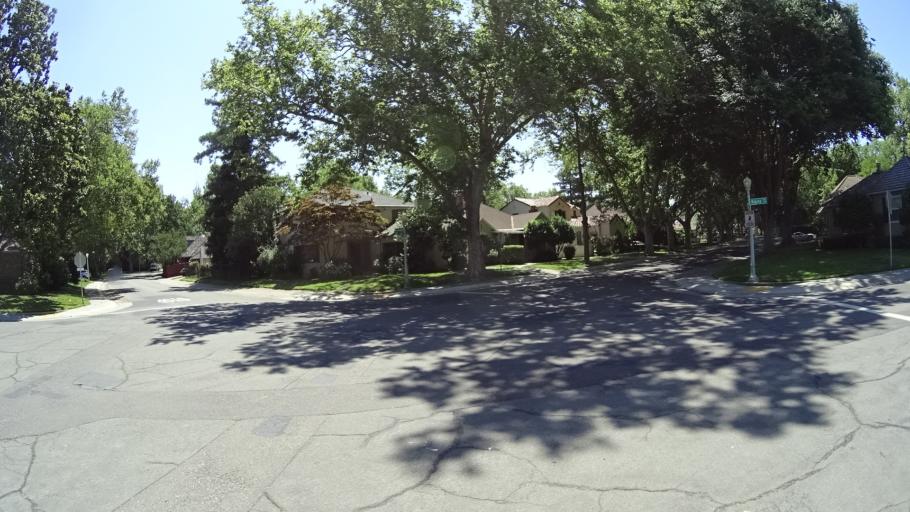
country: US
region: California
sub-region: Sacramento County
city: Sacramento
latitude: 38.5560
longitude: -121.4979
